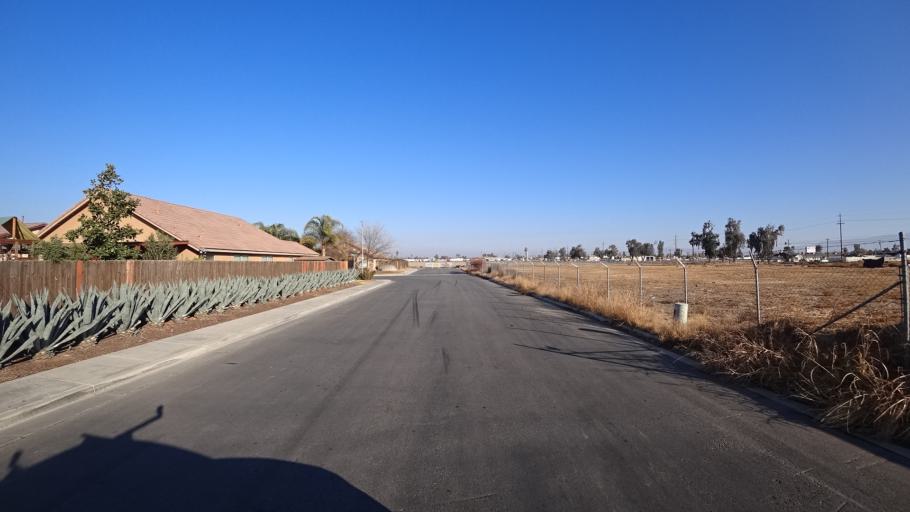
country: US
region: California
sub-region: Kern County
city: Greenfield
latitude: 35.2986
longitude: -119.0046
